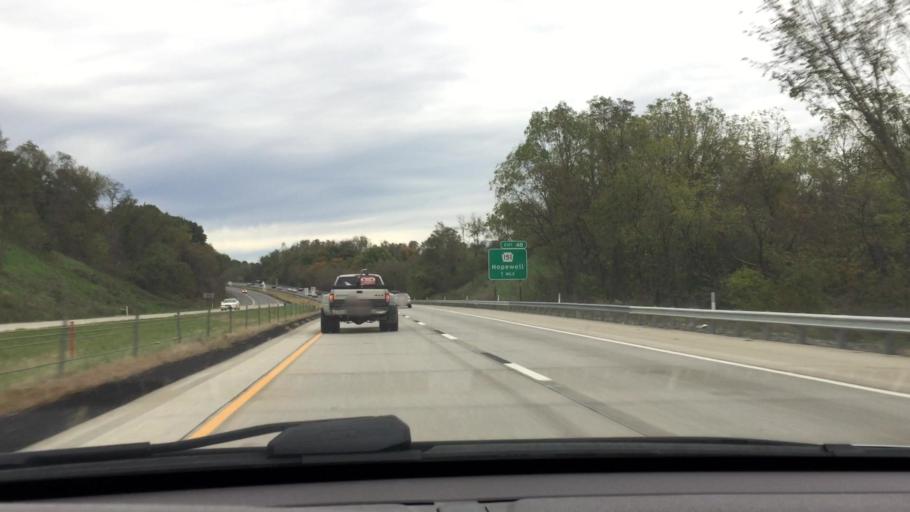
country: US
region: Pennsylvania
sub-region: Allegheny County
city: Carnot-Moon
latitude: 40.5396
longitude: -80.2721
